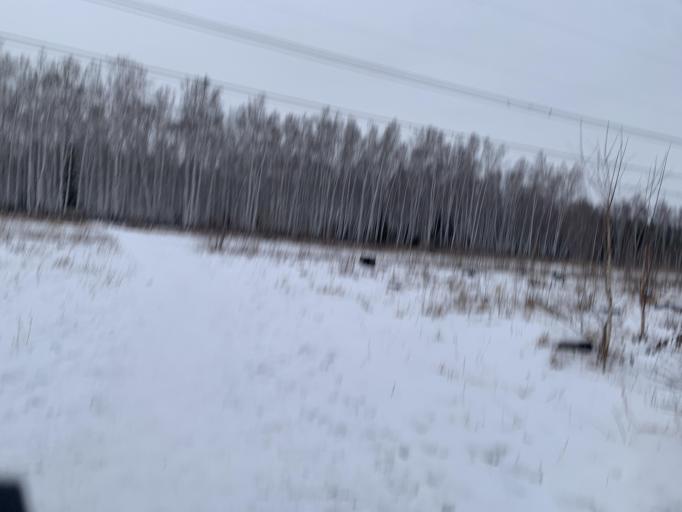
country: RU
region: Chelyabinsk
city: Roshchino
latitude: 55.2037
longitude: 61.2618
